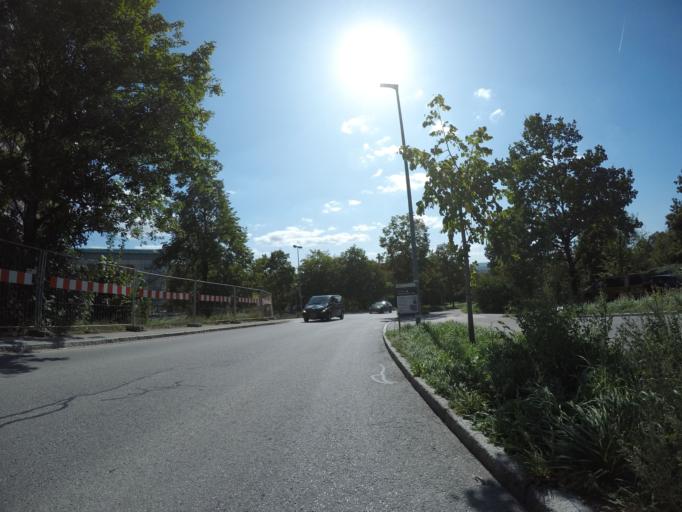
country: DE
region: Baden-Wuerttemberg
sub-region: Tuebingen Region
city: Reutlingen
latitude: 48.5010
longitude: 9.1993
